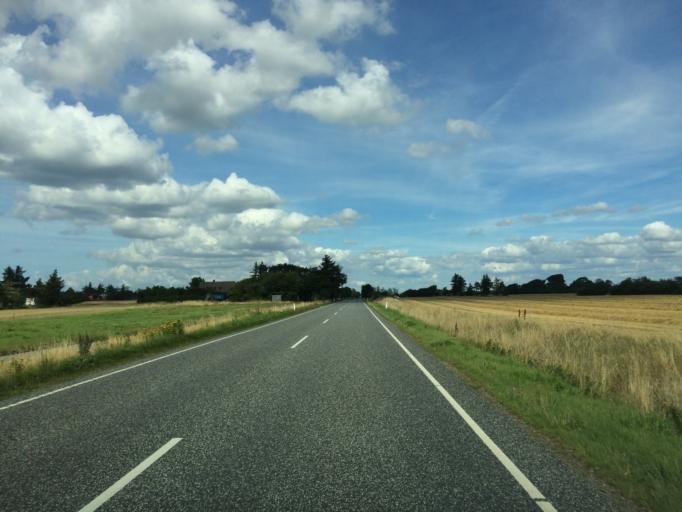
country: DK
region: South Denmark
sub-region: Varde Kommune
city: Oksbol
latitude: 55.8288
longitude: 8.3128
